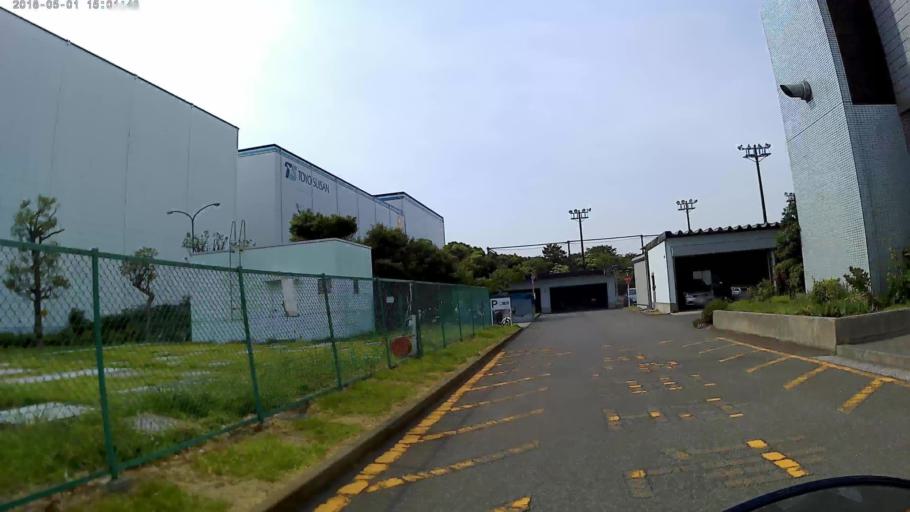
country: JP
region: Kanagawa
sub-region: Kawasaki-shi
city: Kawasaki
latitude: 35.4963
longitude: 139.7627
